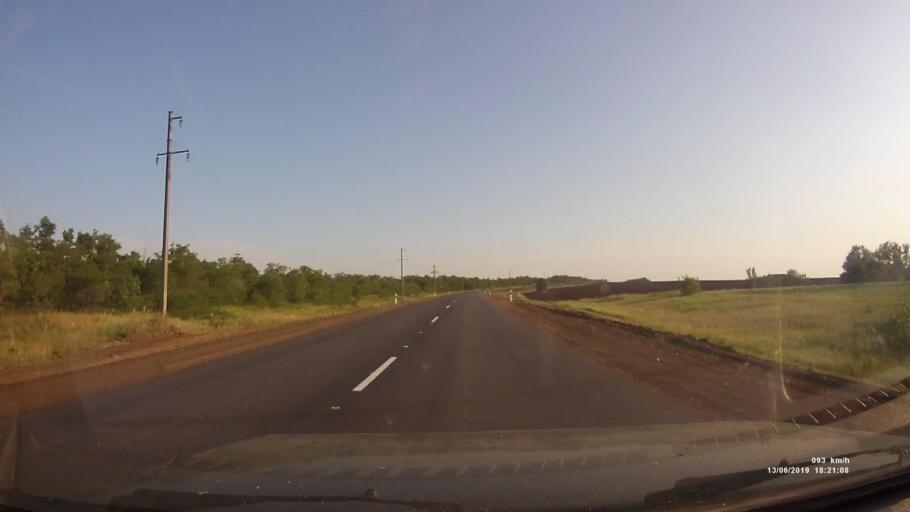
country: RU
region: Rostov
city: Kazanskaya
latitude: 49.8745
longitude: 41.2940
